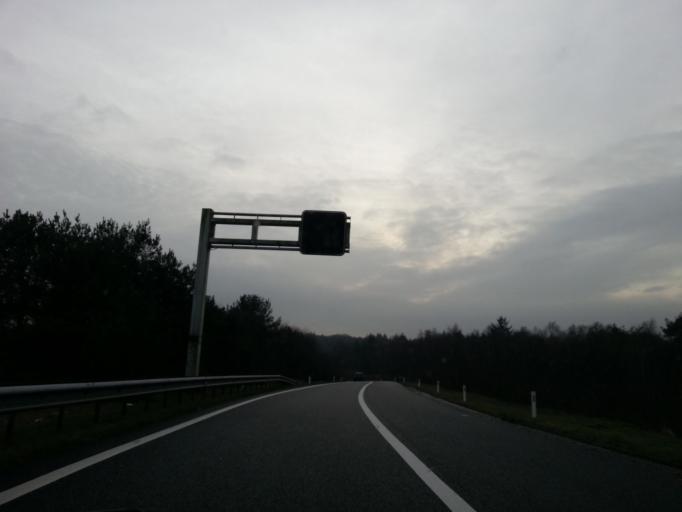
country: NL
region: Gelderland
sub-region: Gemeente Arnhem
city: Burgemeesterswijk
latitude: 52.0205
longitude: 5.9231
